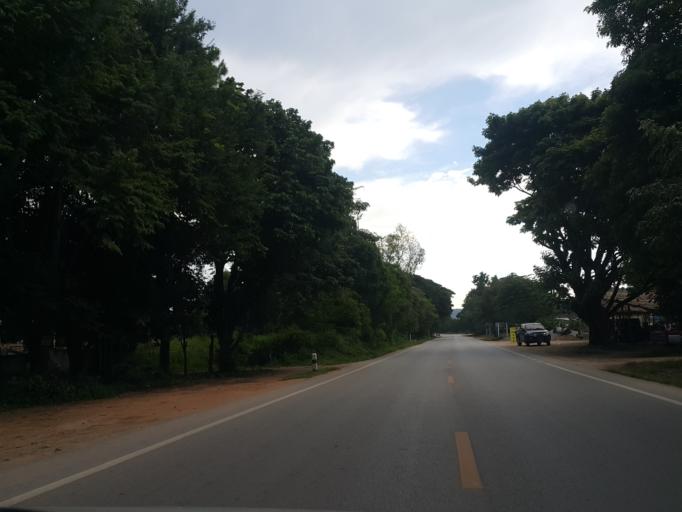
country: TH
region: Chiang Mai
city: Phrao
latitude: 19.3335
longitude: 99.1930
